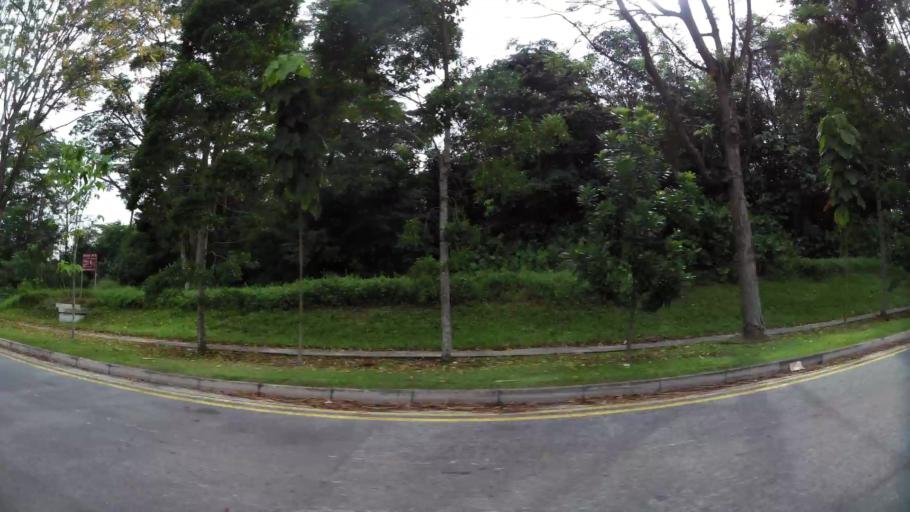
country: MY
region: Johor
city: Johor Bahru
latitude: 1.4170
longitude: 103.7616
